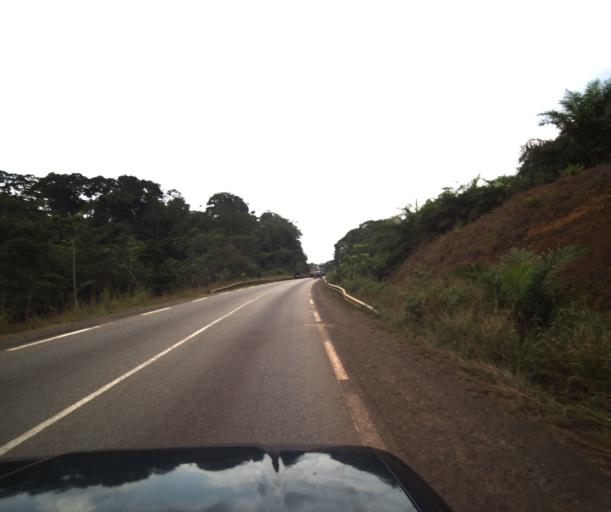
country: CM
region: Littoral
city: Edea
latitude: 3.8145
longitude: 10.3291
